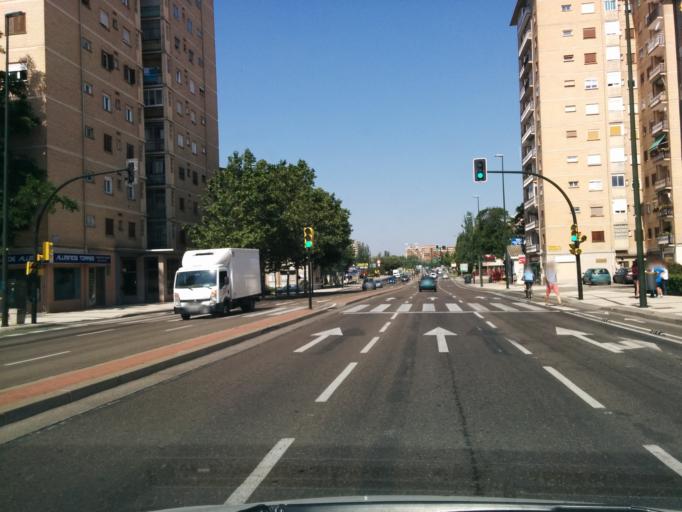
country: ES
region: Aragon
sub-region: Provincia de Zaragoza
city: Zaragoza
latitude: 41.6666
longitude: -0.8739
